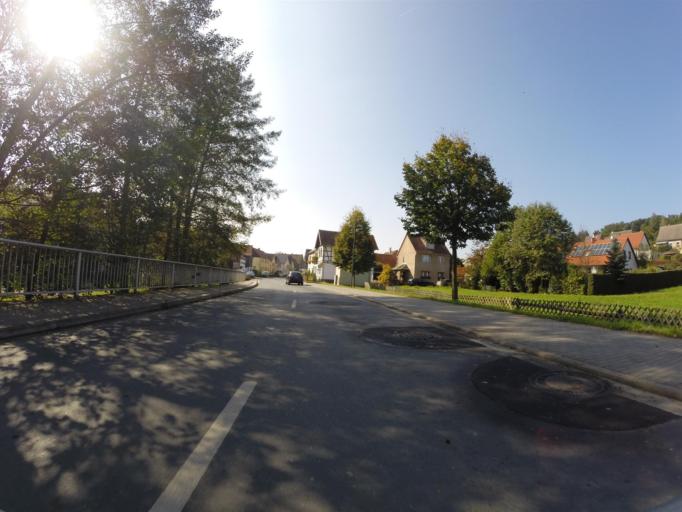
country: DE
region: Thuringia
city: Trobnitz
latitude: 50.8379
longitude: 11.7278
